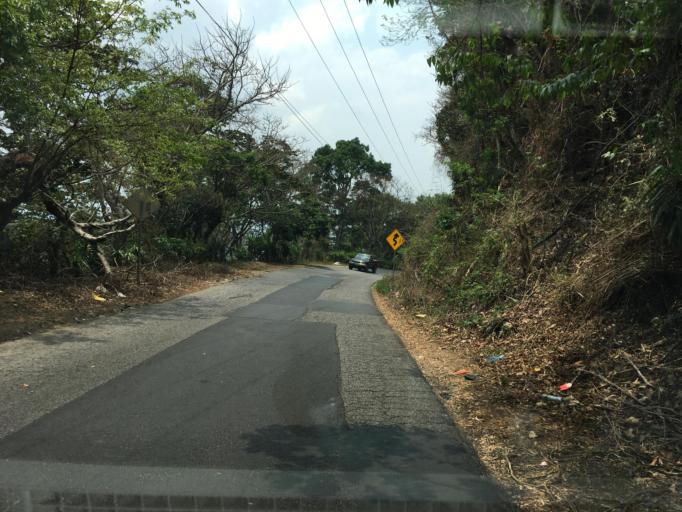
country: GT
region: Escuintla
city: San Vicente Pacaya
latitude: 14.3889
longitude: -90.5512
